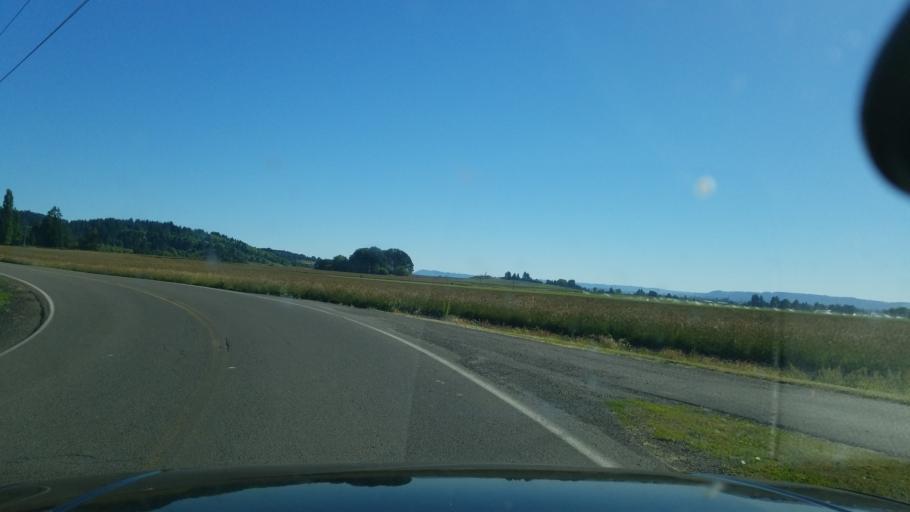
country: US
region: Oregon
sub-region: Yamhill County
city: McMinnville
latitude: 45.2266
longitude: -123.2532
